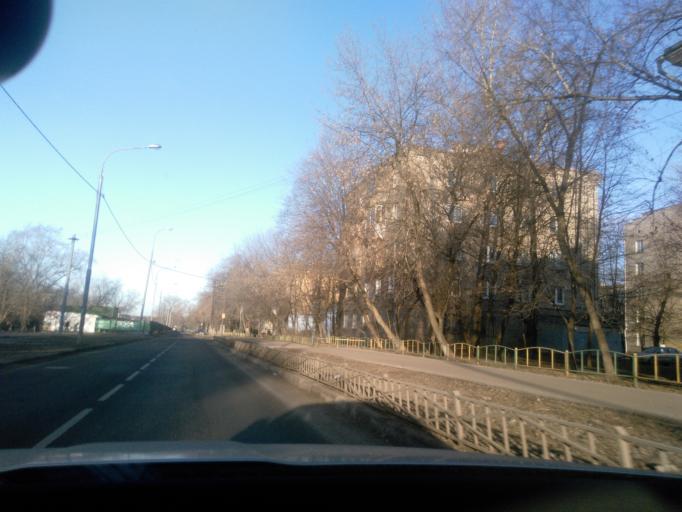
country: RU
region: Moskovskaya
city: Koptevo
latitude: 55.8154
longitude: 37.4944
